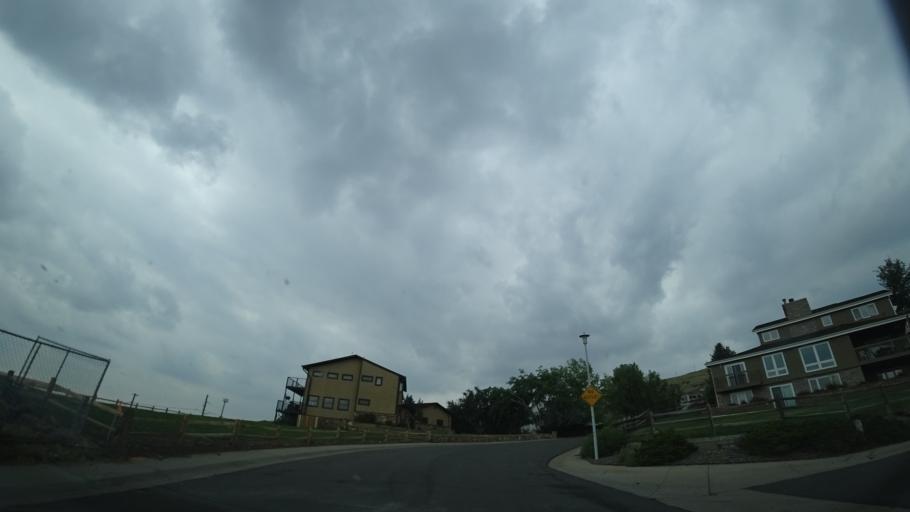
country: US
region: Colorado
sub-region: Jefferson County
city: West Pleasant View
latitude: 39.6996
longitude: -105.1535
